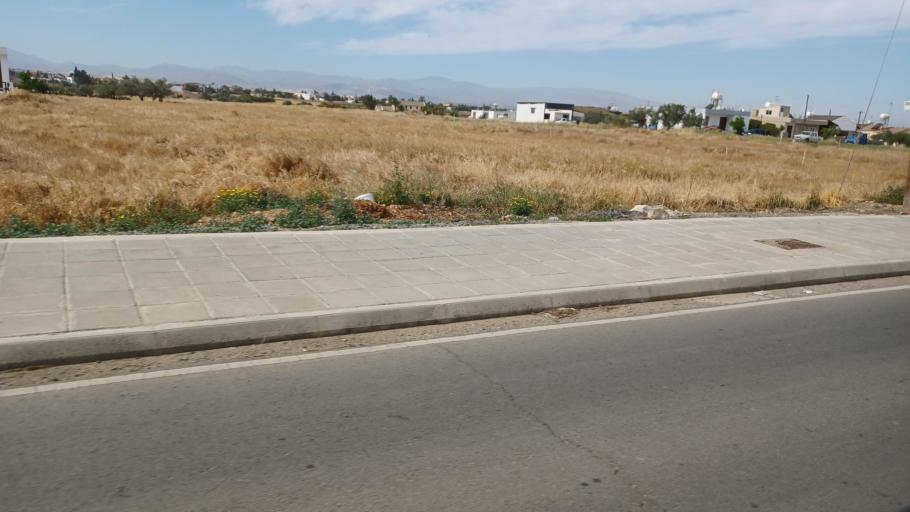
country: CY
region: Lefkosia
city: Kokkinotrimithia
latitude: 35.1553
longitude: 33.1906
